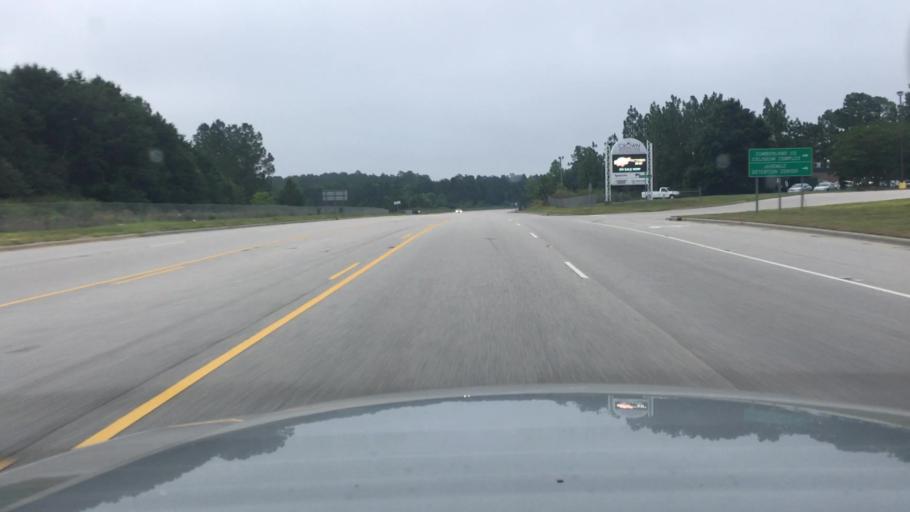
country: US
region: North Carolina
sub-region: Cumberland County
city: Fayetteville
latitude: 35.0186
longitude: -78.8912
